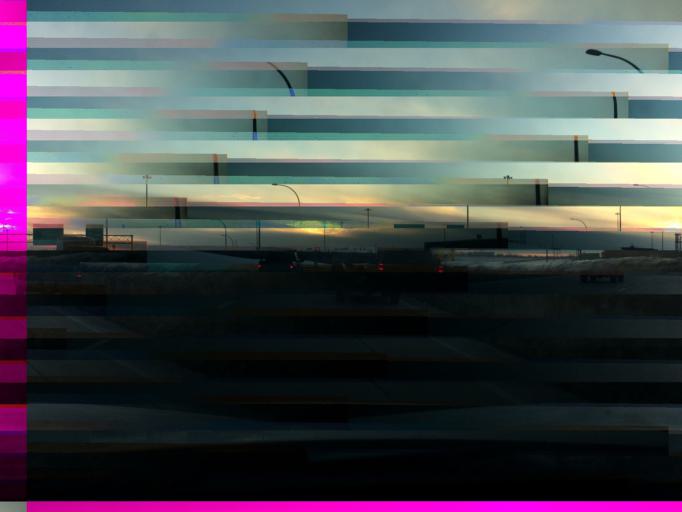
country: CA
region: Quebec
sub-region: Montreal
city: Saint-Leonard
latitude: 45.6079
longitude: -73.5640
